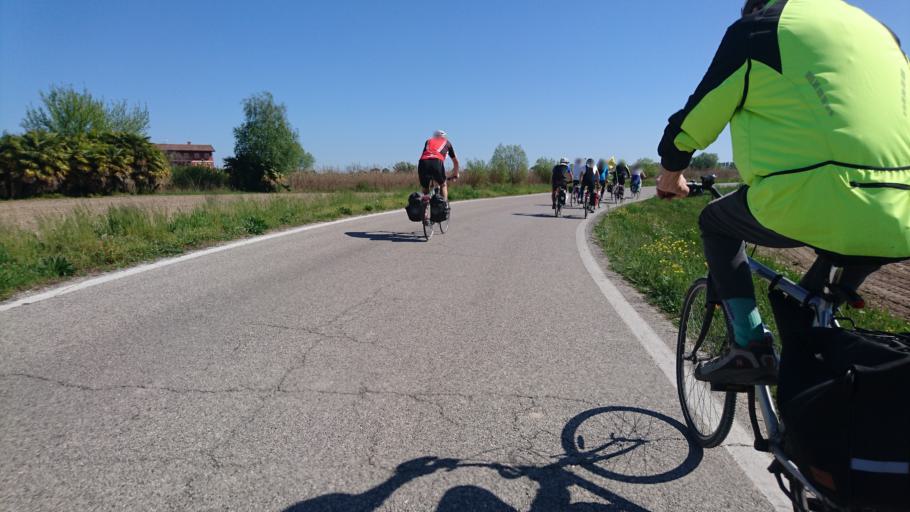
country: IT
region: Veneto
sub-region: Provincia di Venezia
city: Iesolo
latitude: 45.5441
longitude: 12.6112
